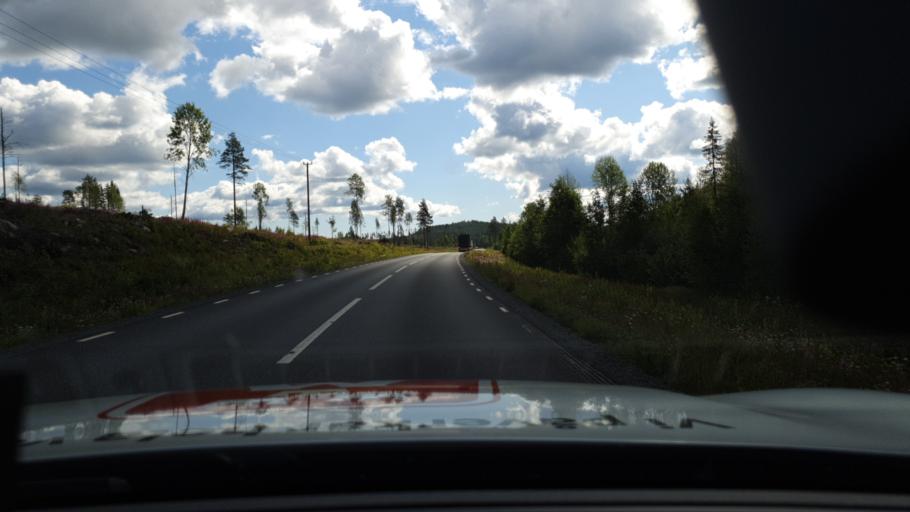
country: SE
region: Norrbotten
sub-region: Bodens Kommun
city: Saevast
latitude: 65.8360
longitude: 21.8560
